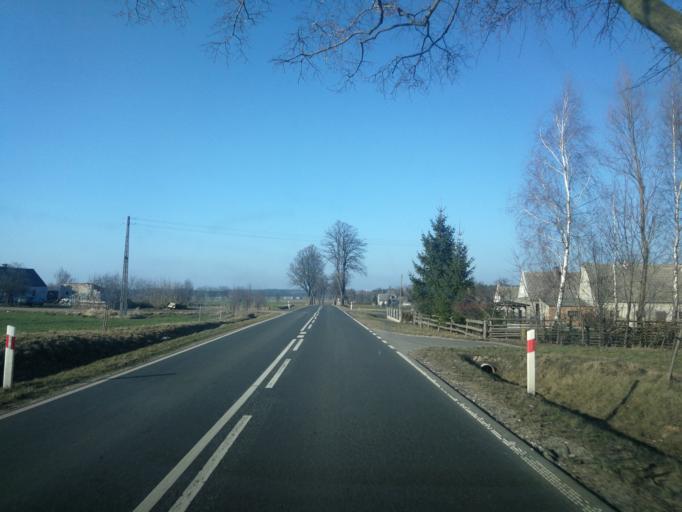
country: PL
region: Warmian-Masurian Voivodeship
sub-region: Powiat dzialdowski
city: Lidzbark
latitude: 53.3544
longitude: 19.8220
